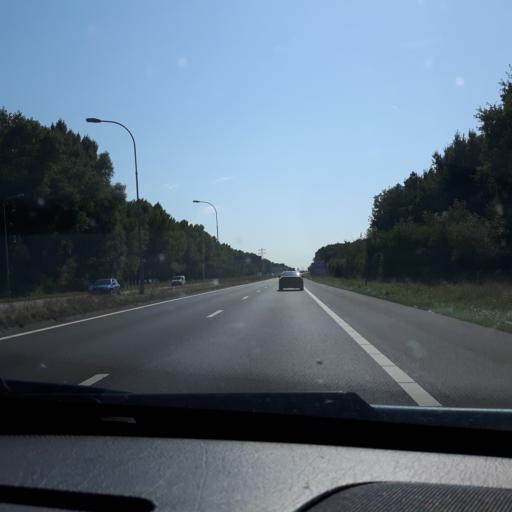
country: NL
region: Zeeland
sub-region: Gemeente Goes
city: Goes
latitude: 51.5044
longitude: 3.8711
